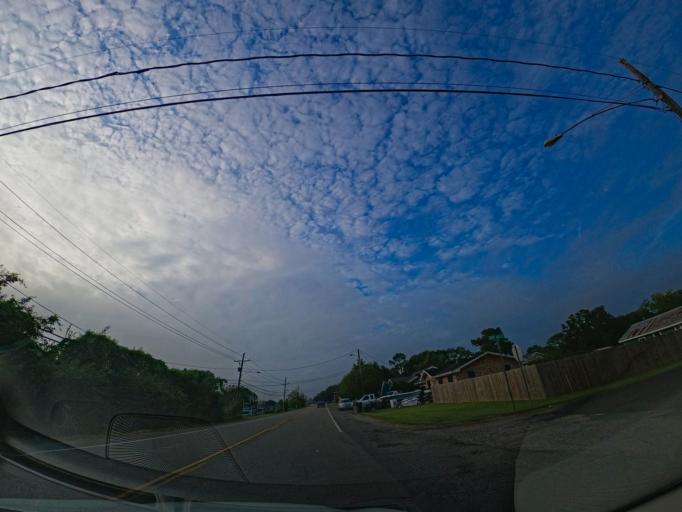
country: US
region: Louisiana
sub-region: Terrebonne Parish
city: Chauvin
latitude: 29.4654
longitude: -90.5895
